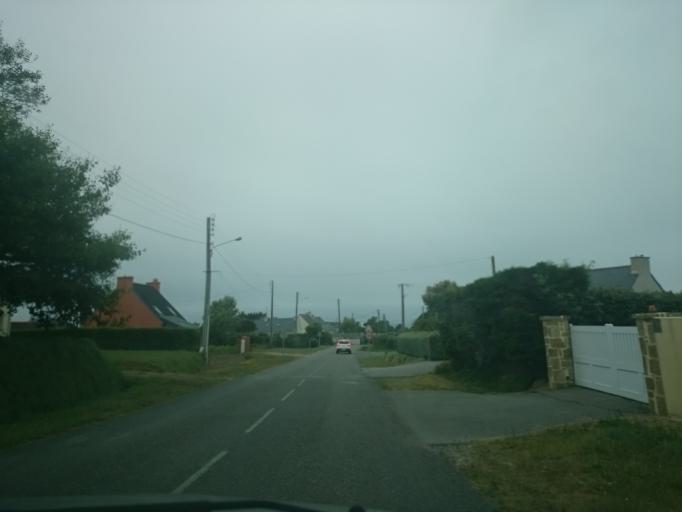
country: FR
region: Brittany
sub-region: Departement du Finistere
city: Saint-Pabu
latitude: 48.5684
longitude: -4.6235
